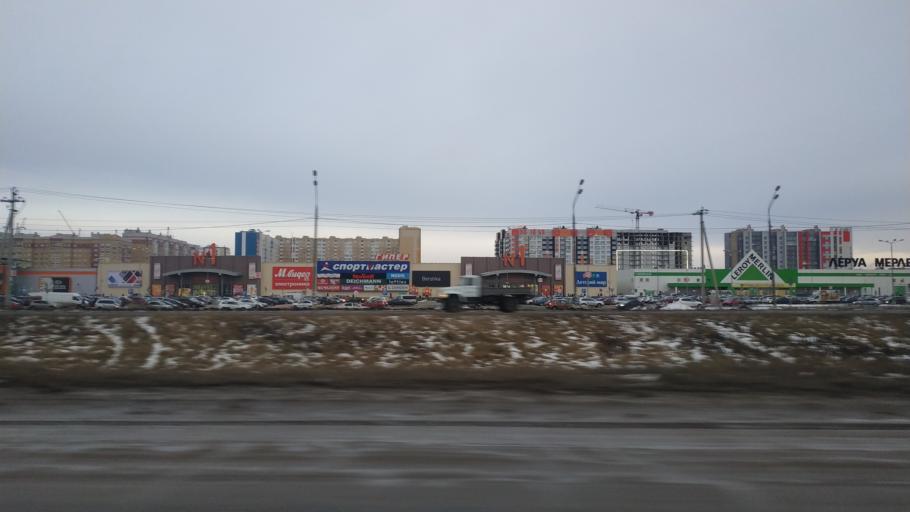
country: RU
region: Tverskaya
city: Tver
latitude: 56.8159
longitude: 35.8809
